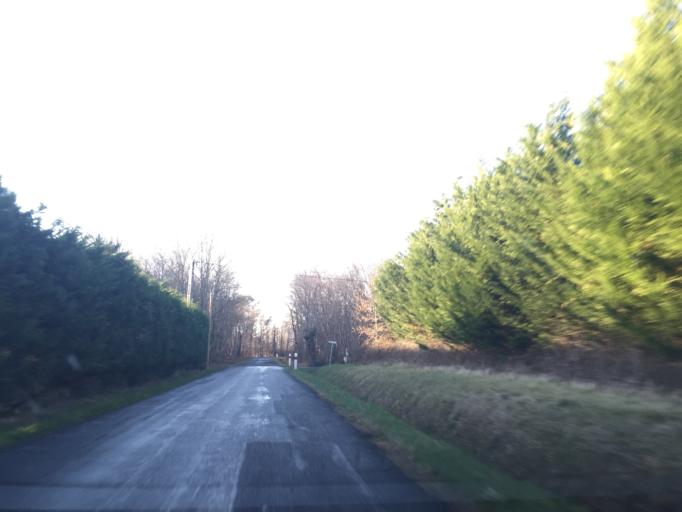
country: FR
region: Aquitaine
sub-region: Departement de la Dordogne
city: Riberac
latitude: 45.2057
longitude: 0.3128
